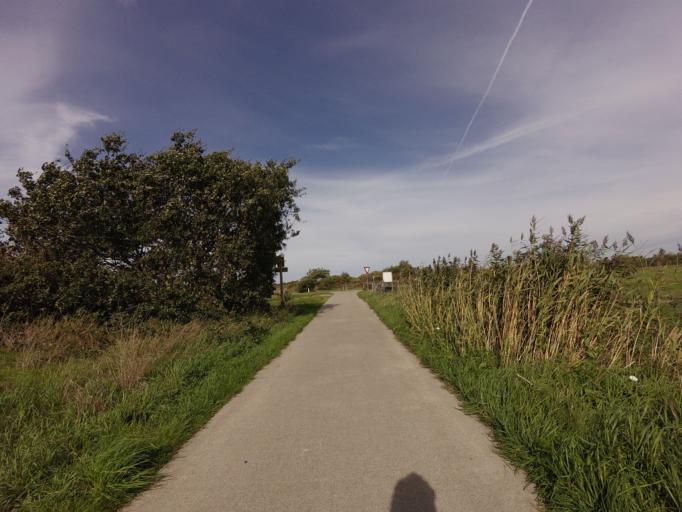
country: NL
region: North Holland
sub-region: Gemeente Texel
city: Den Burg
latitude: 53.1017
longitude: 4.7962
